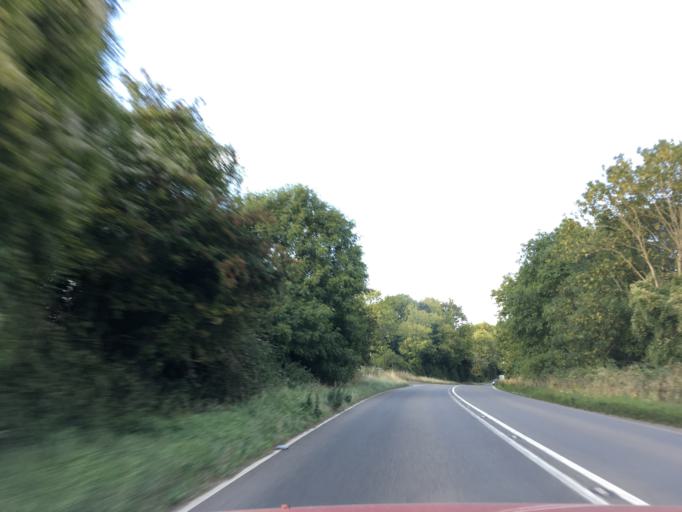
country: GB
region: England
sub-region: Gloucestershire
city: Bourton on the Water
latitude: 51.8658
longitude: -1.7968
